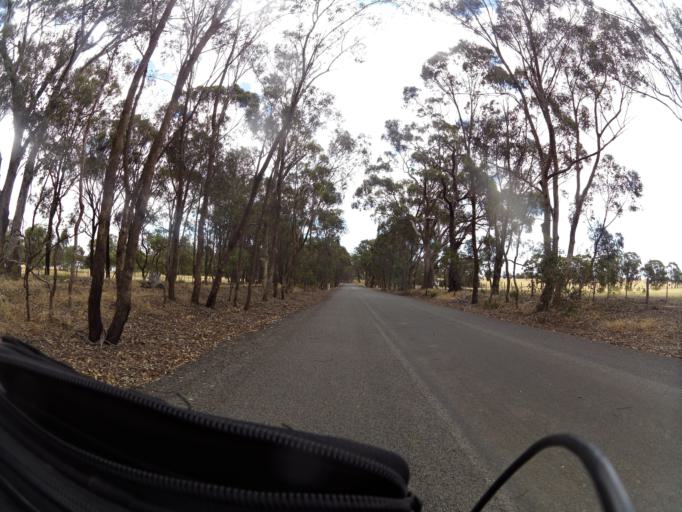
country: AU
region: Victoria
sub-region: Greater Shepparton
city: Shepparton
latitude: -36.7318
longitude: 145.1506
